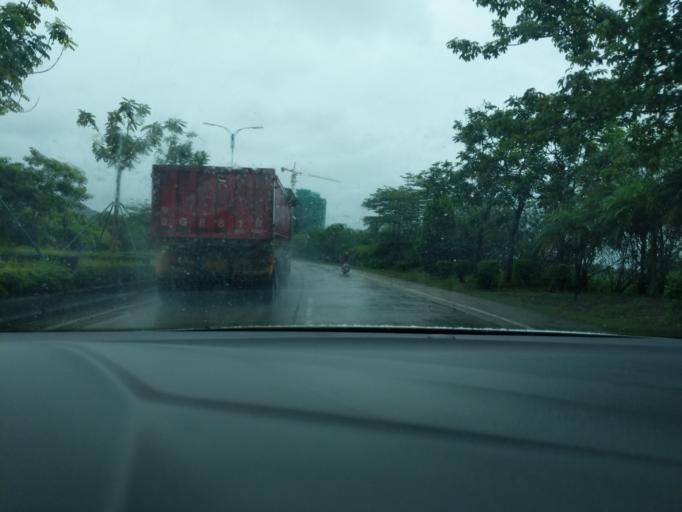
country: CN
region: Guangdong
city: Pingshi
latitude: 22.2099
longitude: 112.3247
